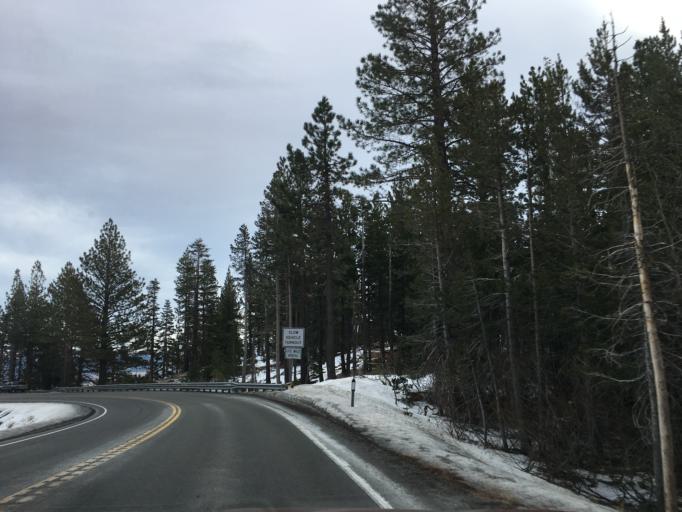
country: US
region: Nevada
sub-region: Washoe County
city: Incline Village
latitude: 39.3311
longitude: -119.8714
